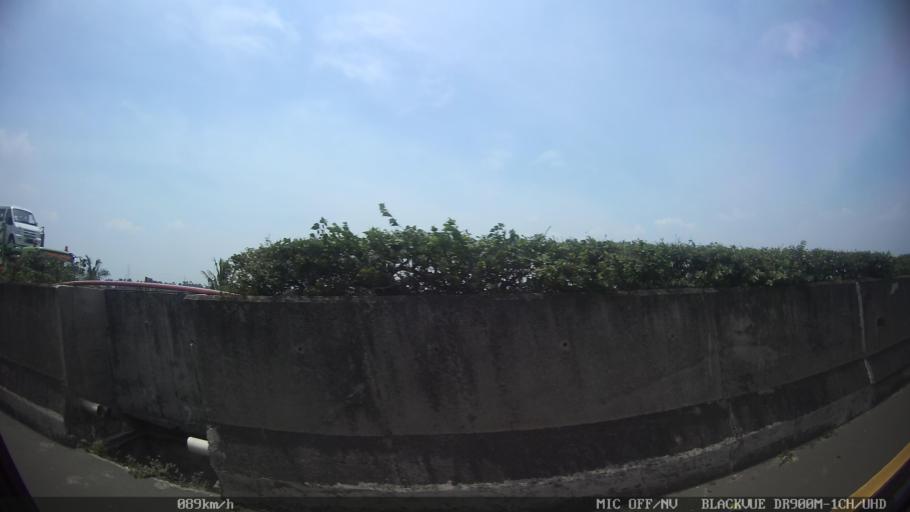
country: ID
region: West Java
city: Kresek
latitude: -6.1770
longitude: 106.3743
